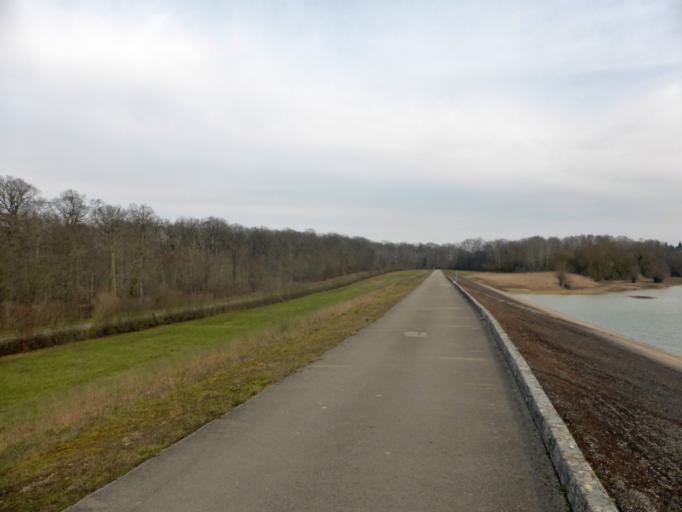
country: FR
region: Champagne-Ardenne
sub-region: Departement de l'Aube
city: Lusigny-sur-Barse
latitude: 48.2707
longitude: 4.3020
